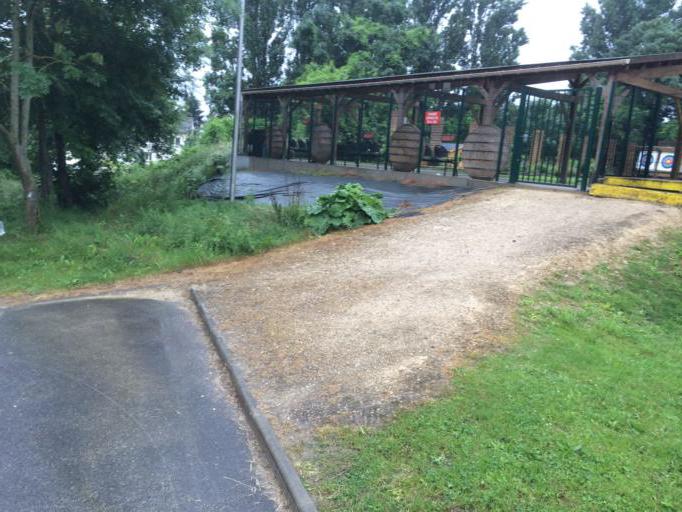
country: FR
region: Ile-de-France
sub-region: Departement de l'Essonne
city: Athis-Mons
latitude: 48.6984
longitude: 2.3792
